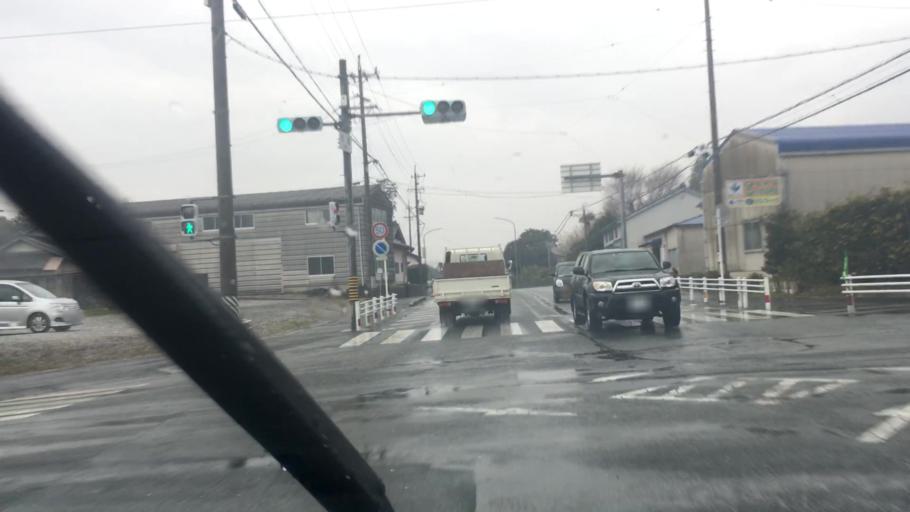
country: JP
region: Aichi
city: Tahara
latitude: 34.6580
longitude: 137.2833
